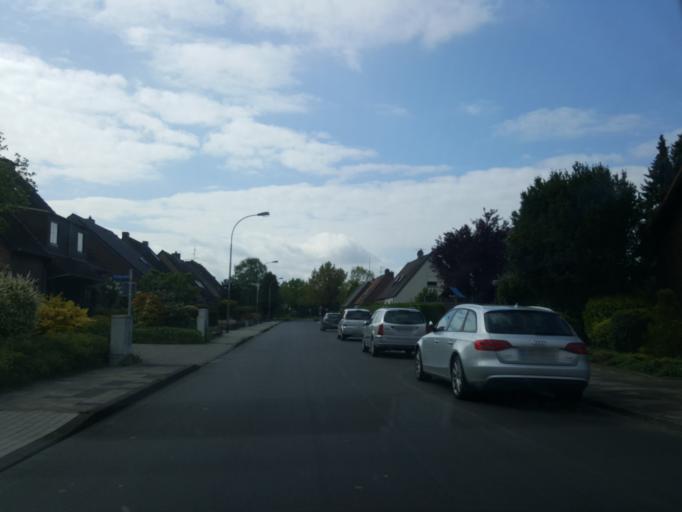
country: DE
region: North Rhine-Westphalia
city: Tonisvorst
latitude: 51.3247
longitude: 6.4758
